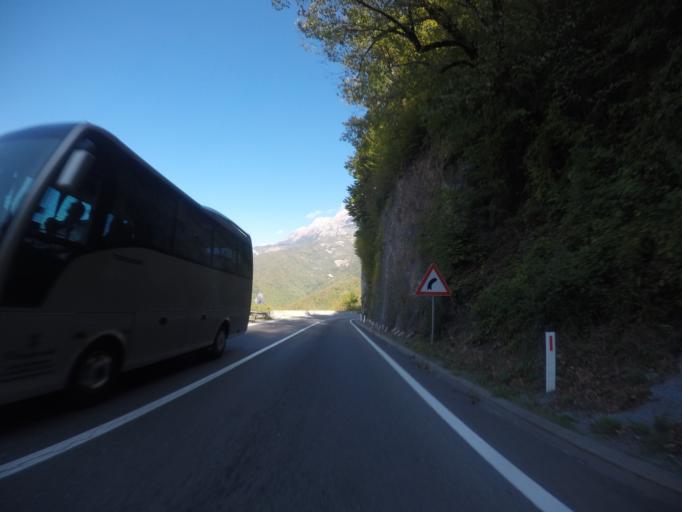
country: ME
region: Opstina Kolasin
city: Kolasin
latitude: 42.8098
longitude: 19.3946
